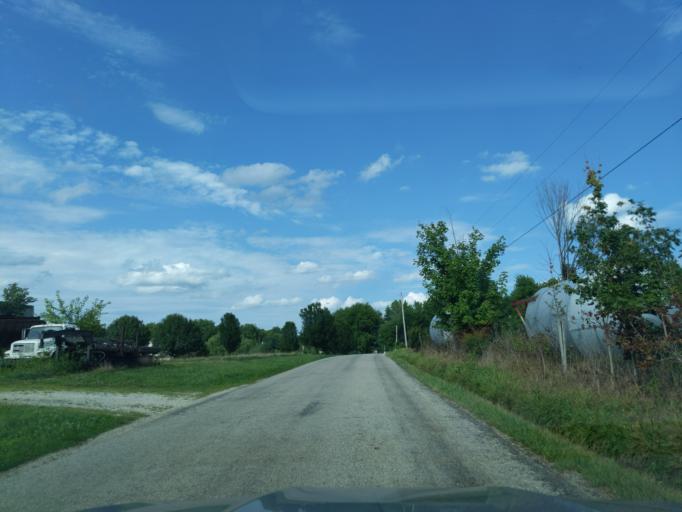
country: US
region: Indiana
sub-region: Ripley County
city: Sunman
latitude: 39.3081
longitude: -85.0781
